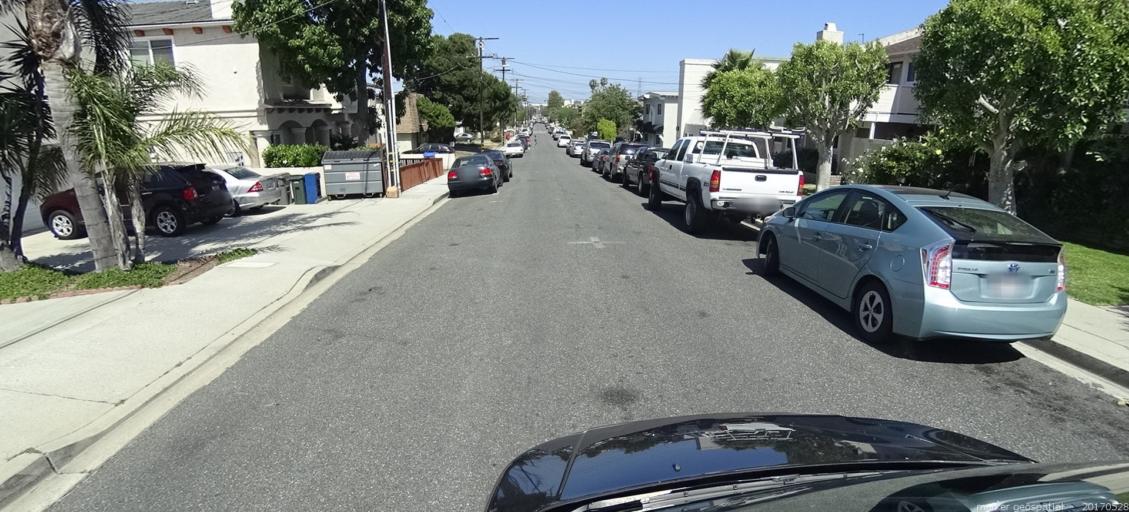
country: US
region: California
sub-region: Los Angeles County
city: Lawndale
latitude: 33.8710
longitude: -118.3705
